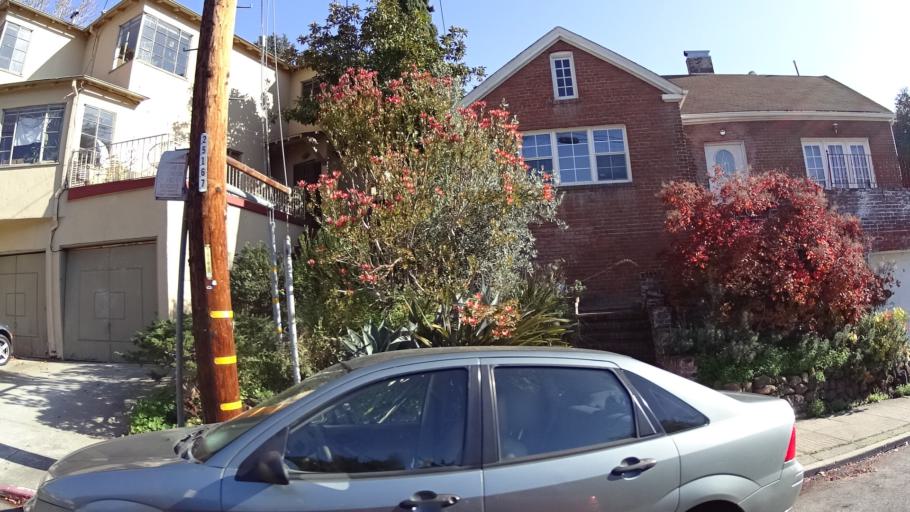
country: US
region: California
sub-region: Alameda County
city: Piedmont
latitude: 37.8045
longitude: -122.2380
